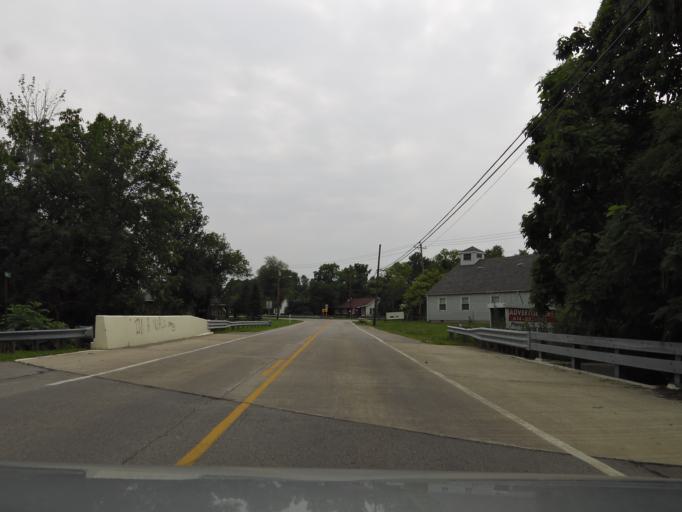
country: US
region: Ohio
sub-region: Clinton County
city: Blanchester
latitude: 39.3071
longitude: -83.9104
